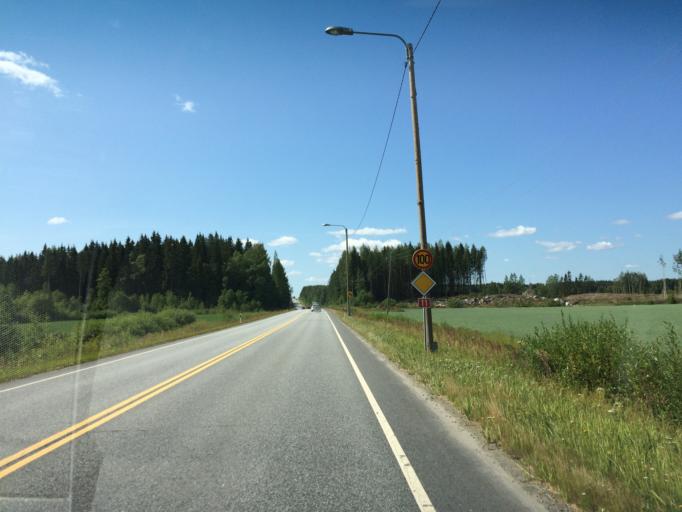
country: FI
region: Pirkanmaa
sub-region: Lounais-Pirkanmaa
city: Kiikoinen
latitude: 61.4815
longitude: 22.6147
